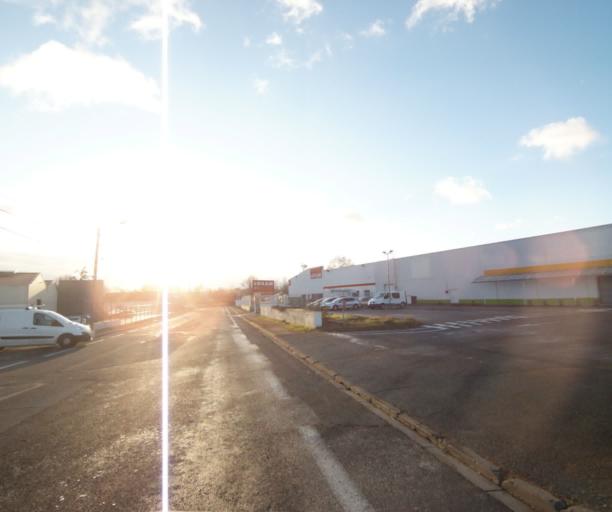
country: FR
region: Rhone-Alpes
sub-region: Departement de la Loire
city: Le Coteau
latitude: 46.0458
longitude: 4.0856
